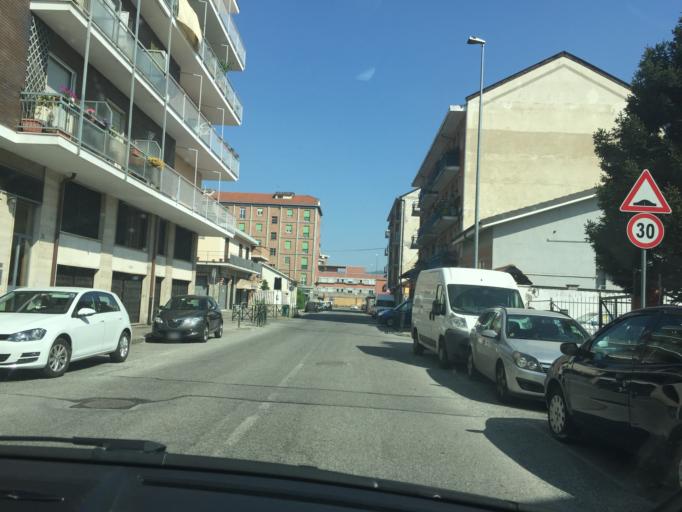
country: IT
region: Piedmont
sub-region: Provincia di Torino
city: Lesna
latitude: 45.0558
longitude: 7.6220
